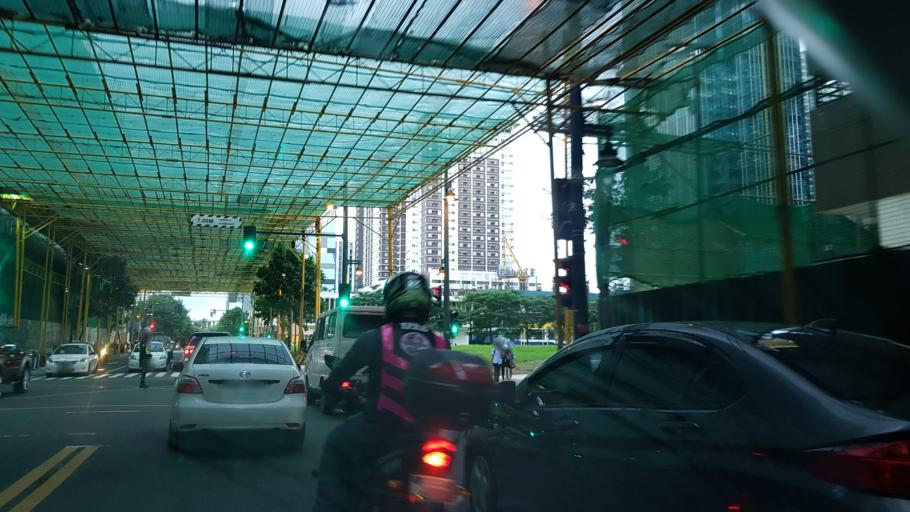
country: PH
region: Metro Manila
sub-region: Makati City
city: Makati City
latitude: 14.5547
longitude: 121.0531
